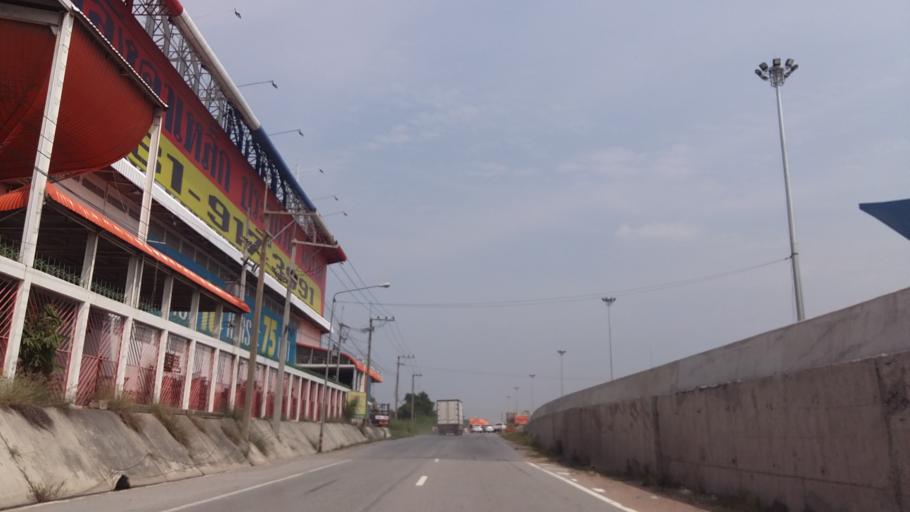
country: TH
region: Chon Buri
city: Chon Buri
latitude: 13.3064
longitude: 100.9933
